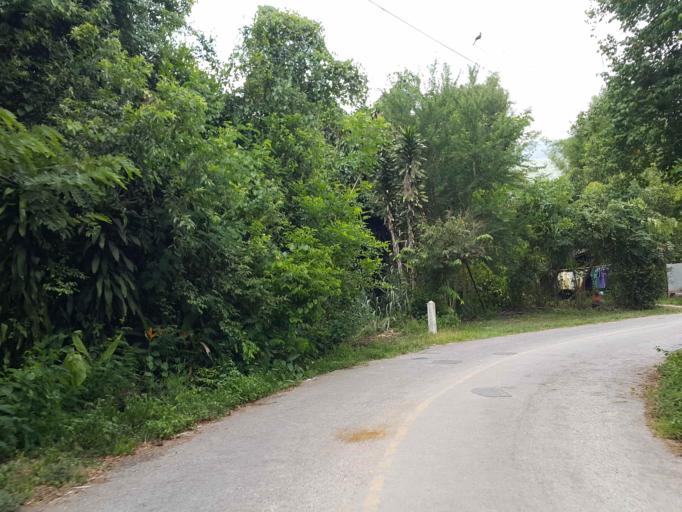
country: TH
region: Chiang Mai
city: Hang Dong
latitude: 18.7596
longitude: 98.9099
